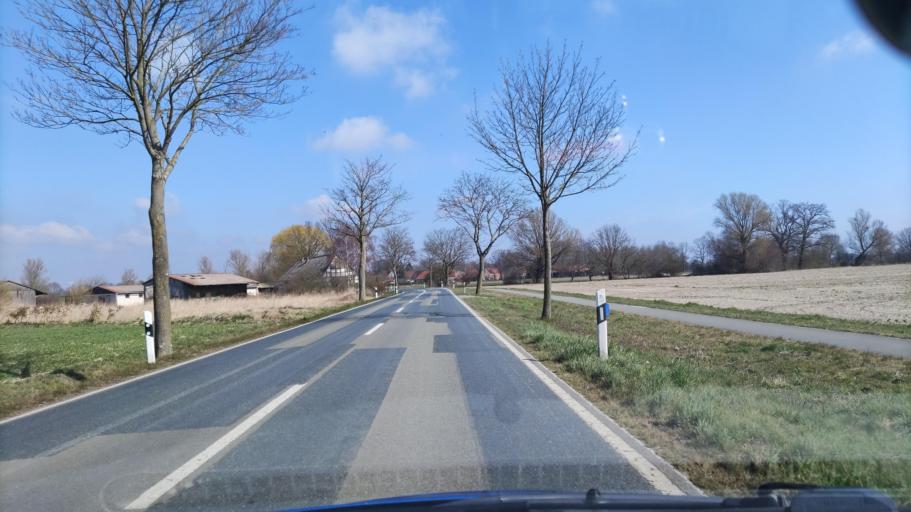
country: DE
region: Lower Saxony
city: Wustrow
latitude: 52.9465
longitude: 11.1302
